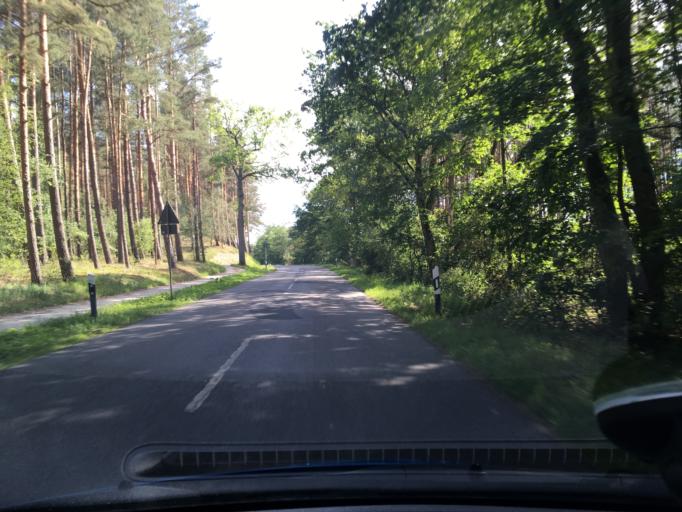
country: DE
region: Lower Saxony
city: Neu Darchau
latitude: 53.2944
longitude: 10.9290
